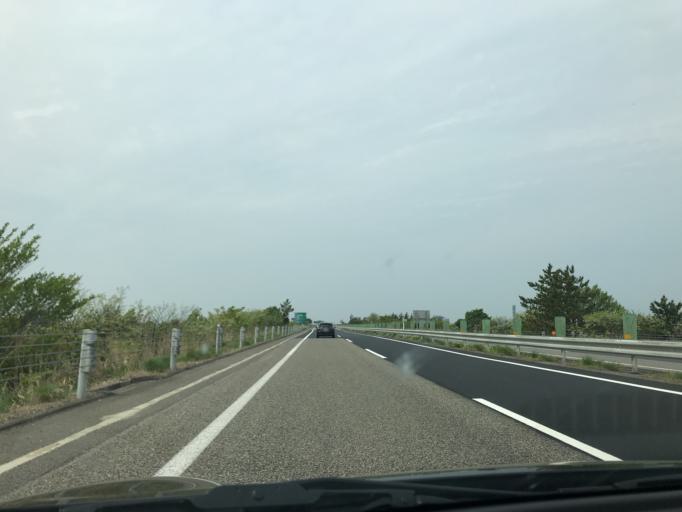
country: JP
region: Niigata
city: Kameda-honcho
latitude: 37.8764
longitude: 139.0648
